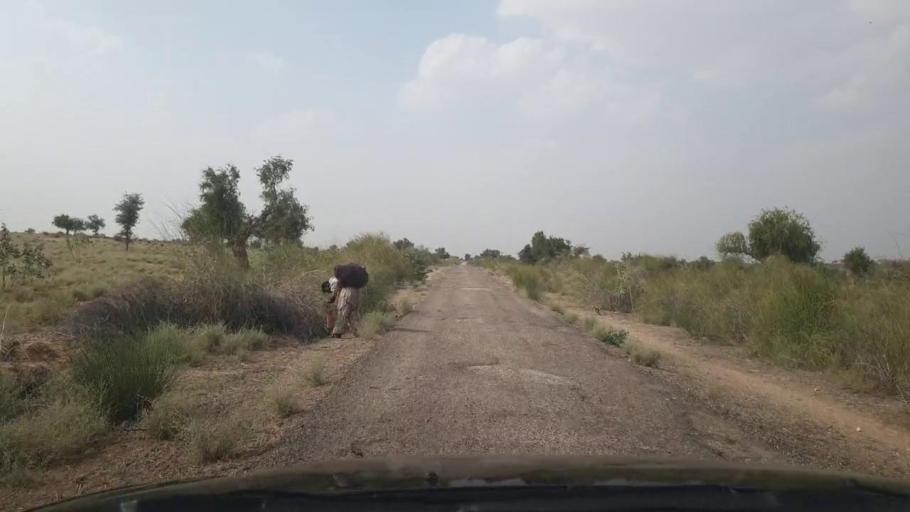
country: PK
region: Sindh
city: Islamkot
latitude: 24.9754
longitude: 70.5862
